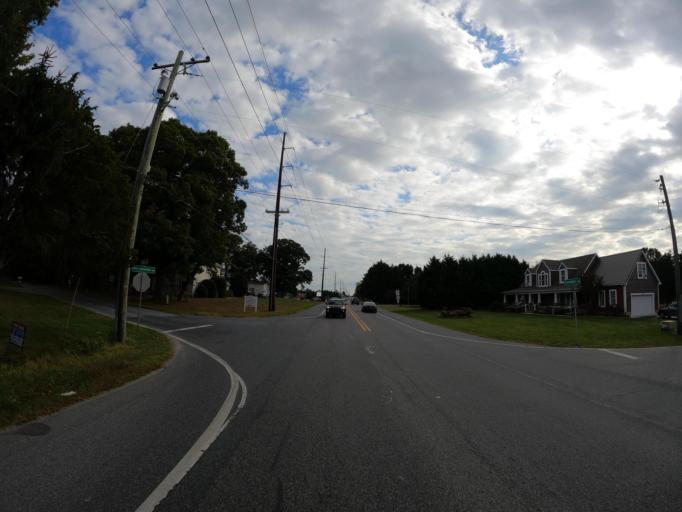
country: US
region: Delaware
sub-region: Sussex County
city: Milton
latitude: 38.7342
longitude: -75.2388
